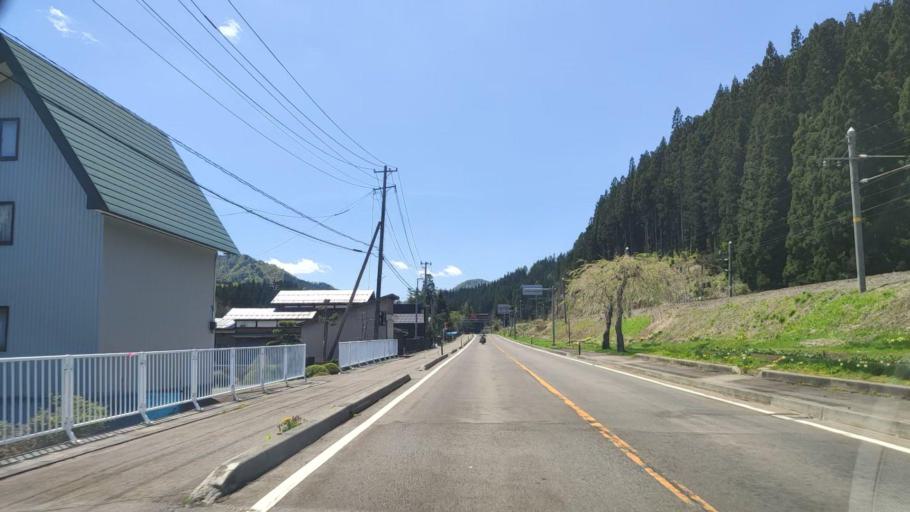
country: JP
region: Akita
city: Yuzawa
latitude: 39.0467
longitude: 140.3983
